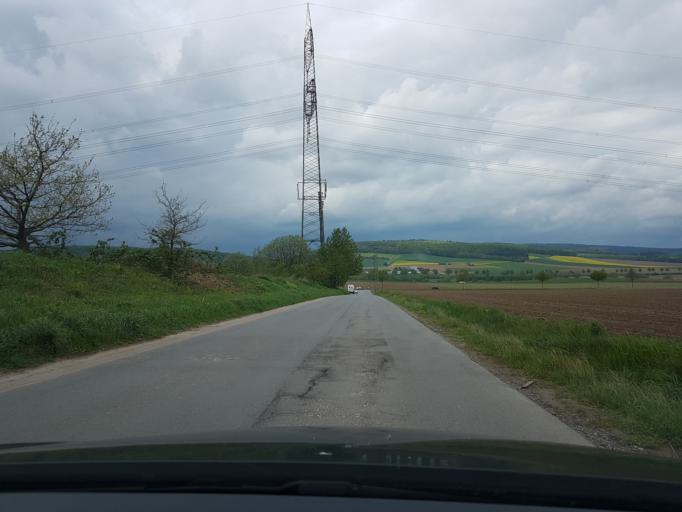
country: DE
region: Lower Saxony
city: Hameln
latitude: 52.1075
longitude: 9.4323
